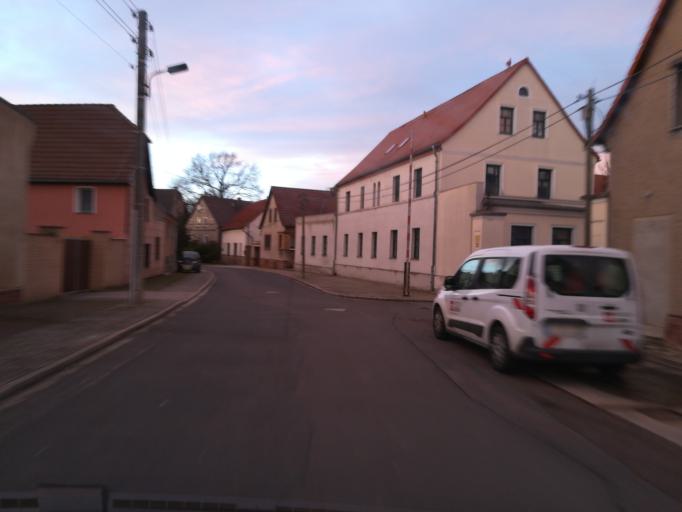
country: DE
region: Saxony-Anhalt
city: Brehna
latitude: 51.5408
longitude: 12.2258
